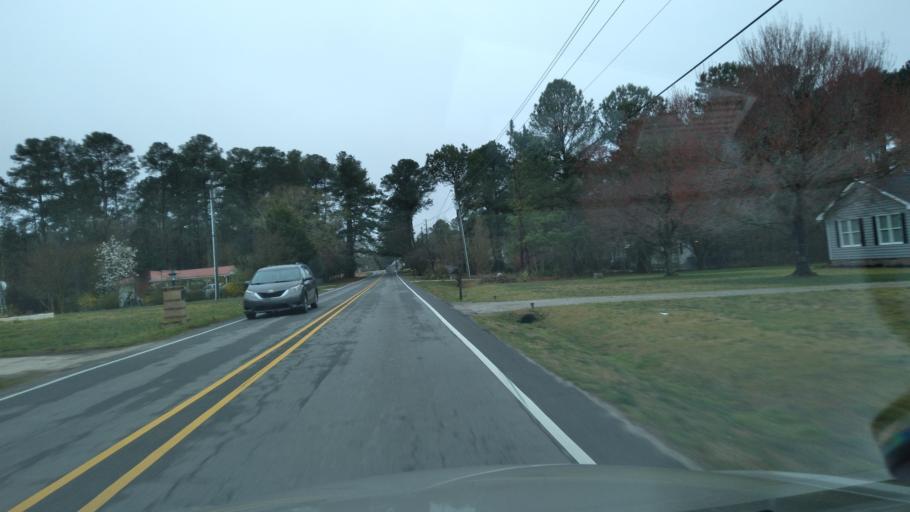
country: US
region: North Carolina
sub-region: Wake County
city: Knightdale
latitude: 35.7825
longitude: -78.4881
